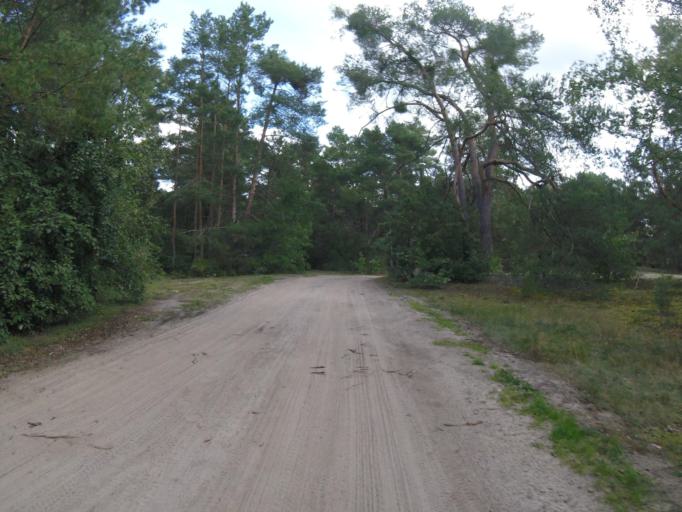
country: DE
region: Brandenburg
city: Mittenwalde
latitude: 52.2215
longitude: 13.5709
